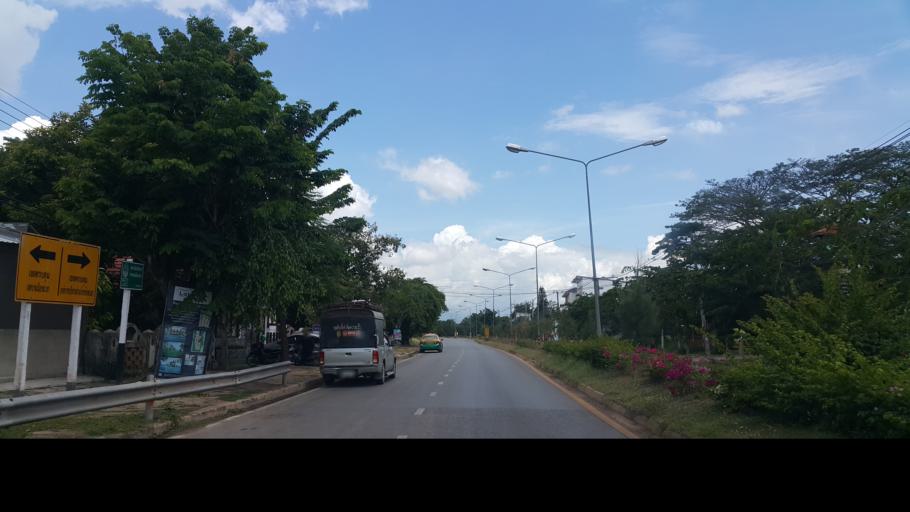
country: TH
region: Phayao
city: Phayao
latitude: 19.1784
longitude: 99.8877
